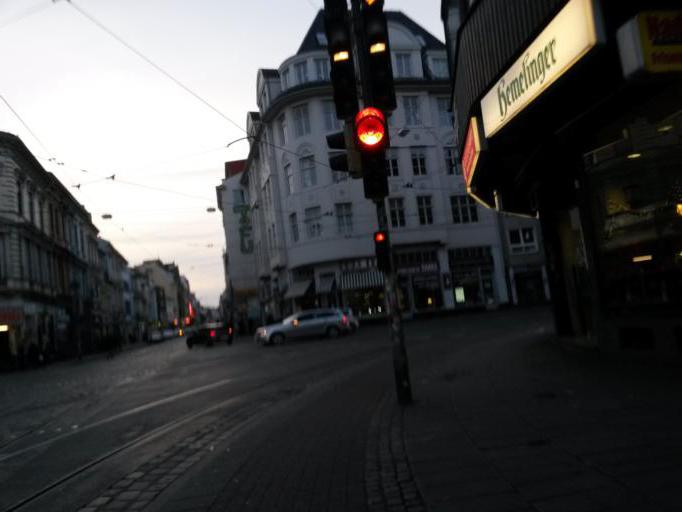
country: DE
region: Bremen
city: Bremen
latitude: 53.0731
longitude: 8.8237
